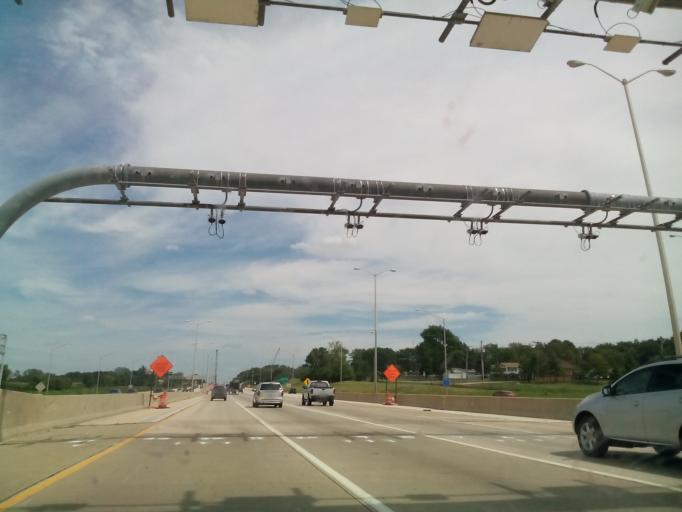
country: US
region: Illinois
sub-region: Kane County
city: North Aurora
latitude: 41.7968
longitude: -88.3091
